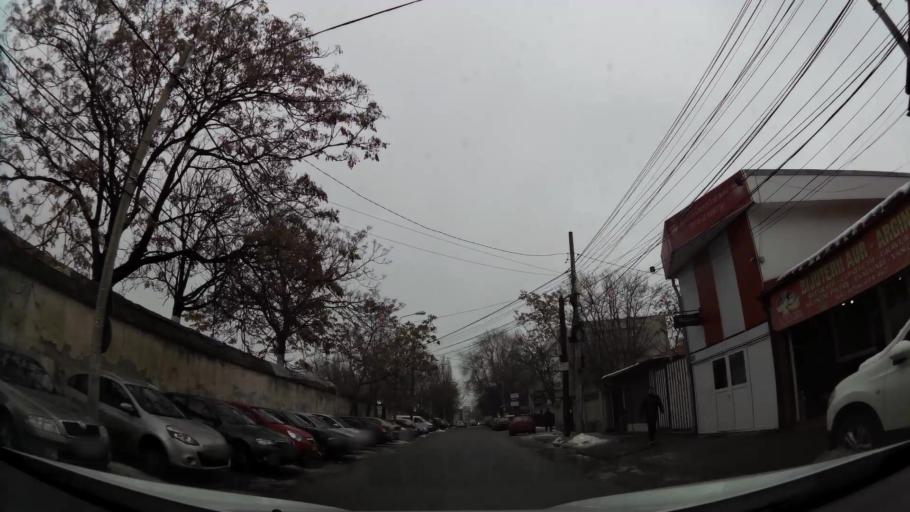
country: RO
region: Ilfov
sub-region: Comuna Popesti-Leordeni
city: Popesti-Leordeni
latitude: 44.4116
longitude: 26.1588
